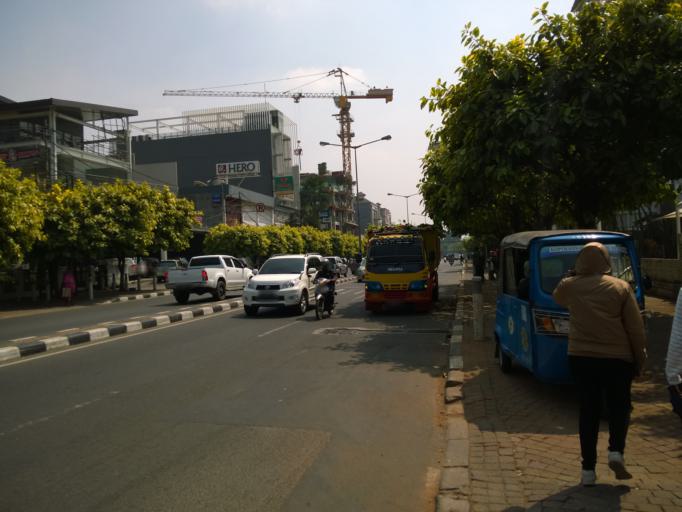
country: ID
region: Jakarta Raya
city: Jakarta
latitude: -6.1984
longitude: 106.8285
